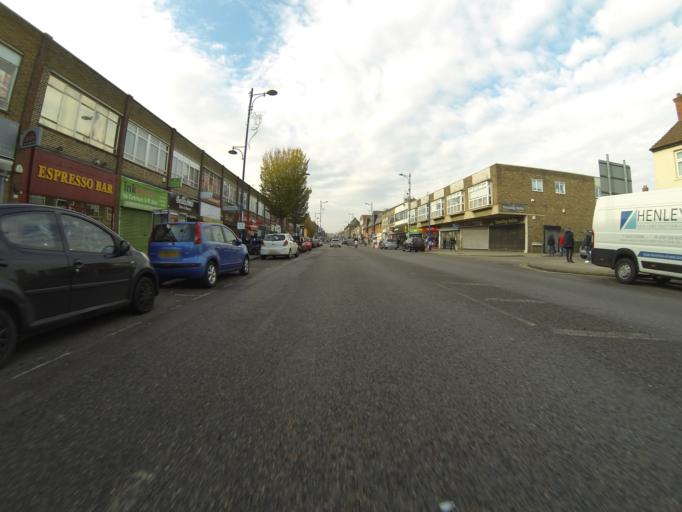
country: GB
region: England
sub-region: Greater London
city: Welling
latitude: 51.4628
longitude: 0.1058
